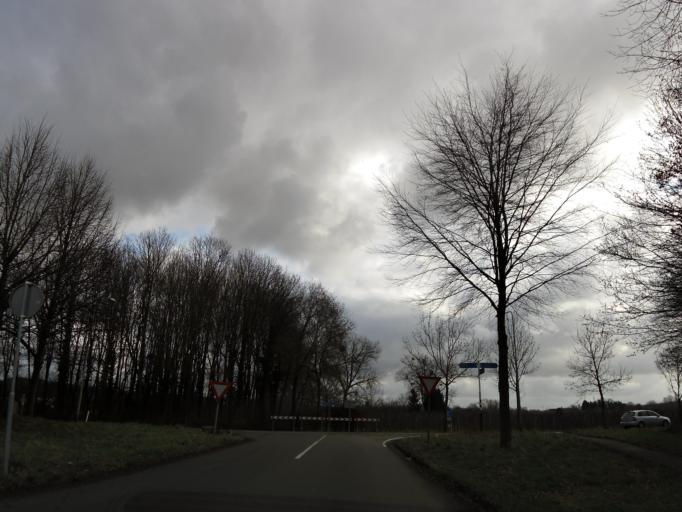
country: NL
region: Limburg
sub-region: Gemeente Meerssen
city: Meerssen
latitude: 50.8907
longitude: 5.7248
